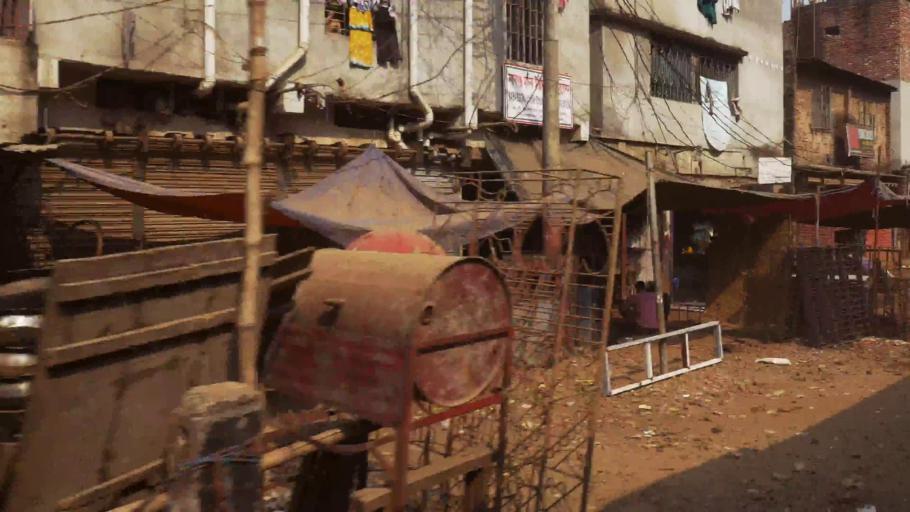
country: BD
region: Dhaka
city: Paltan
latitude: 23.7520
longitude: 90.3964
